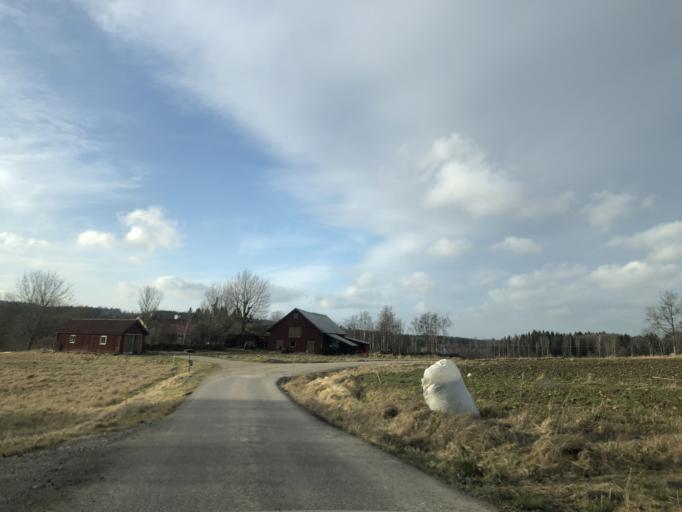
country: SE
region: Vaestra Goetaland
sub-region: Ulricehamns Kommun
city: Ulricehamn
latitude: 57.8121
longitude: 13.3593
